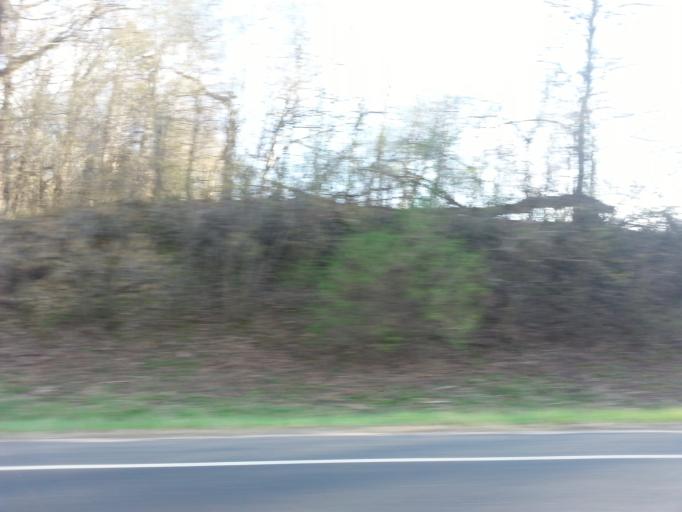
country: US
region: Wisconsin
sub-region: Pierce County
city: River Falls
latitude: 44.8332
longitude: -92.6407
